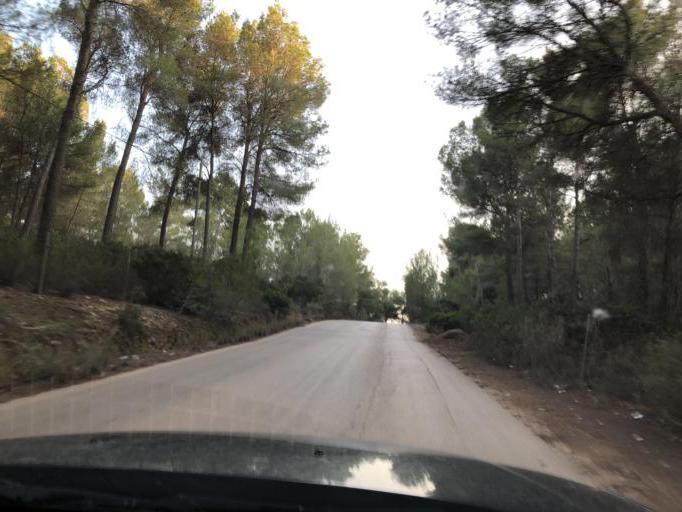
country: ES
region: Balearic Islands
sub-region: Illes Balears
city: Santa Ponsa
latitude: 39.5371
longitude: 2.4816
